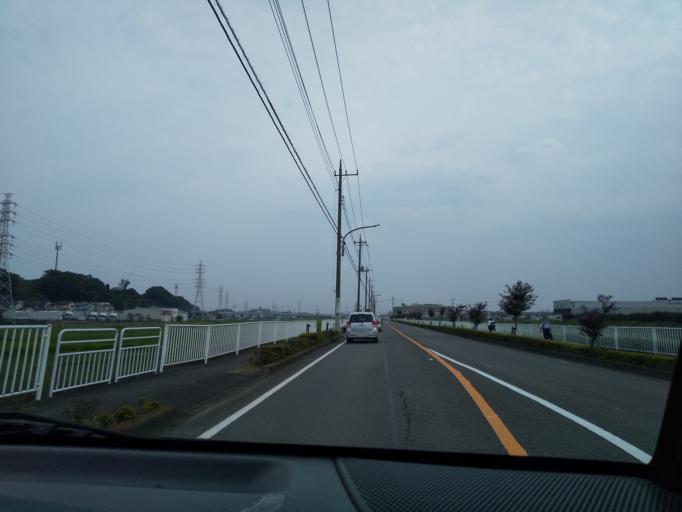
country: JP
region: Kanagawa
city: Atsugi
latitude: 35.4348
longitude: 139.3904
